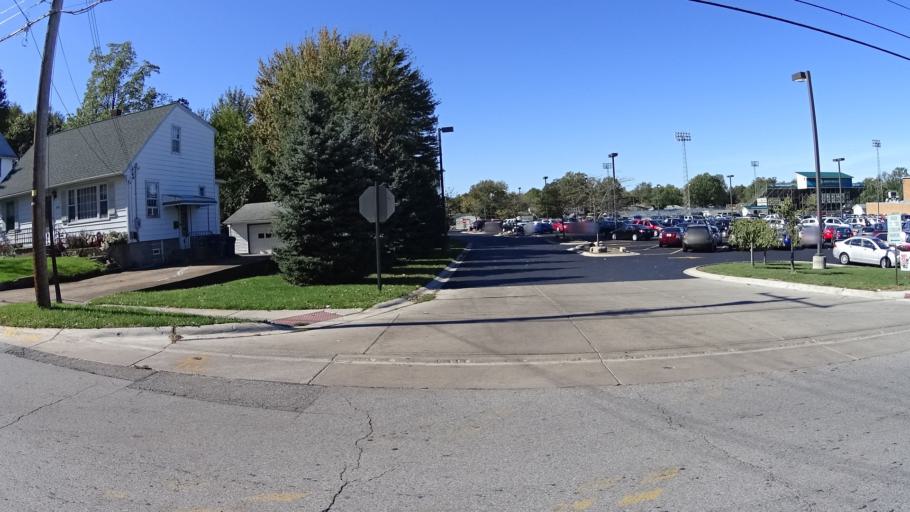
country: US
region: Ohio
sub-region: Lorain County
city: Amherst
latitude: 41.4022
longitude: -82.2216
